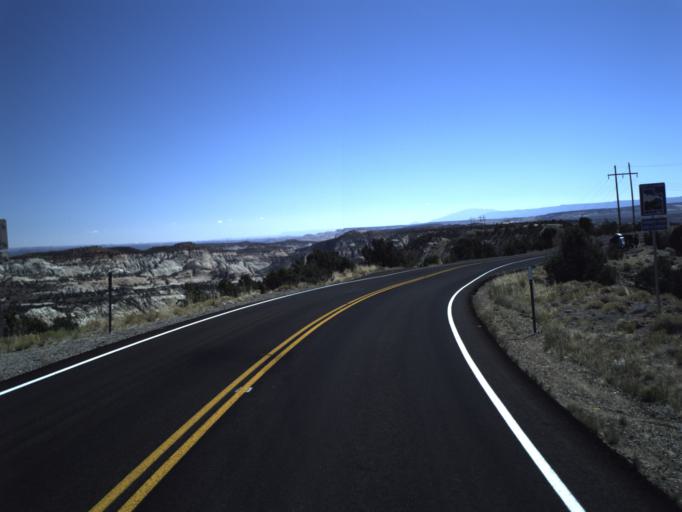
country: US
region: Utah
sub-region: Wayne County
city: Loa
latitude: 37.8422
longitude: -111.4224
